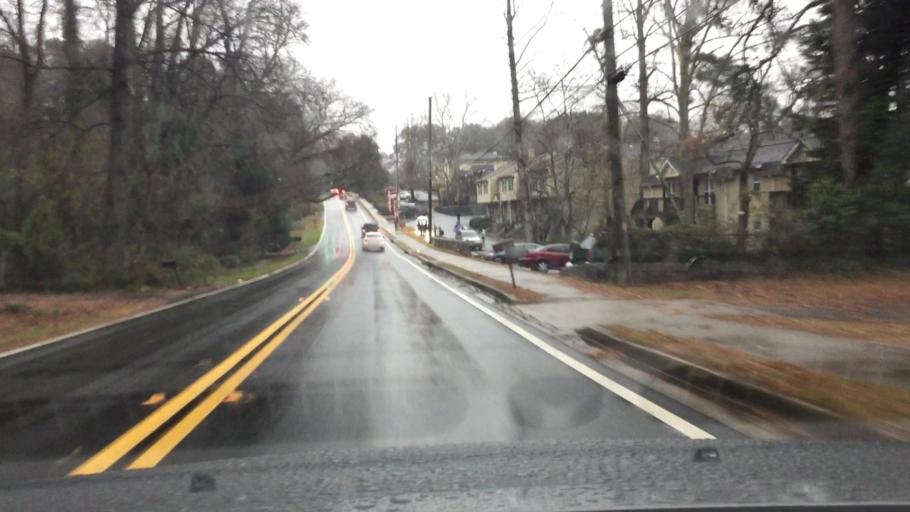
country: US
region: Georgia
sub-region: Cobb County
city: Fair Oaks
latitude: 33.8992
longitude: -84.5646
